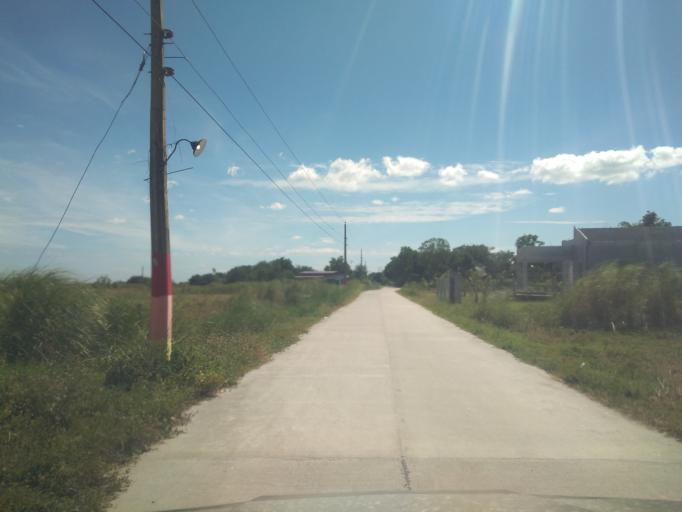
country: PH
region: Central Luzon
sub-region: Province of Pampanga
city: San Basilio
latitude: 15.0349
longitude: 120.6048
